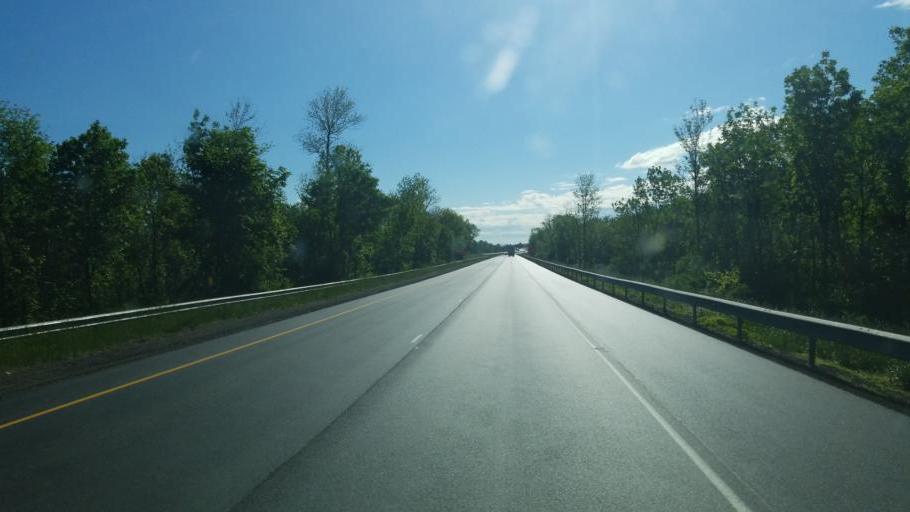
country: US
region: New York
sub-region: Genesee County
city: Bergen
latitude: 43.0288
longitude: -77.9266
